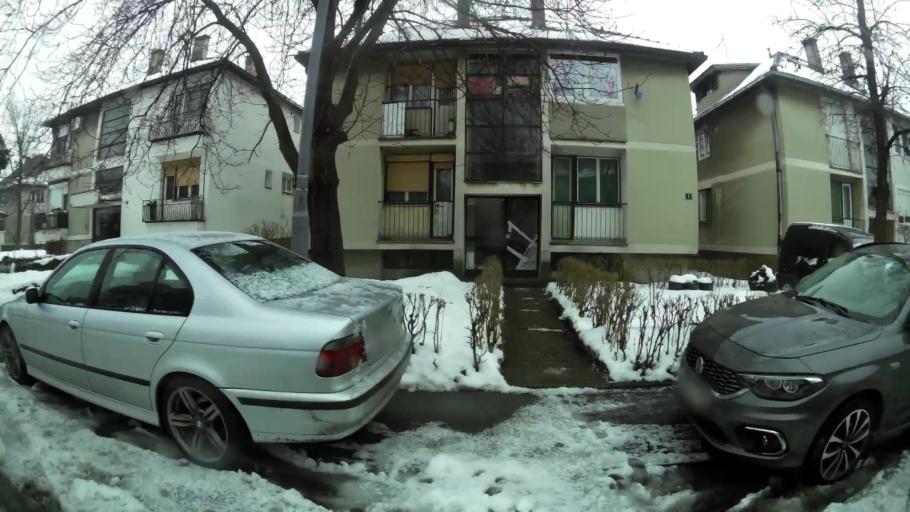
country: RS
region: Central Serbia
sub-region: Belgrade
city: Zemun
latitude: 44.8723
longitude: 20.3268
